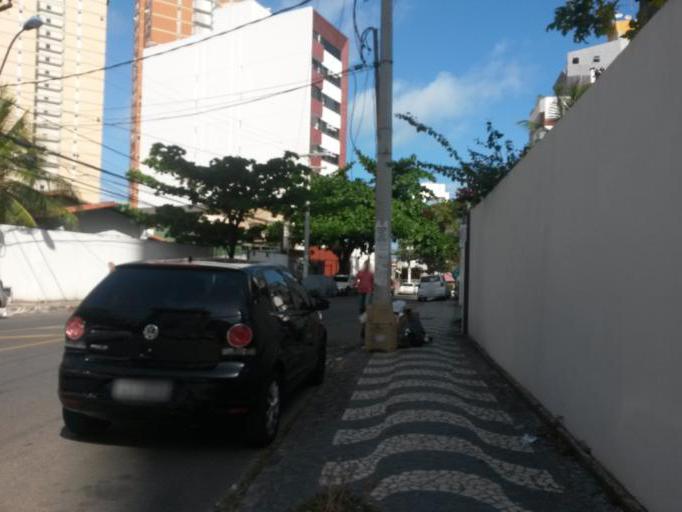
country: BR
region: Bahia
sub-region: Salvador
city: Salvador
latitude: -13.0003
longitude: -38.4630
